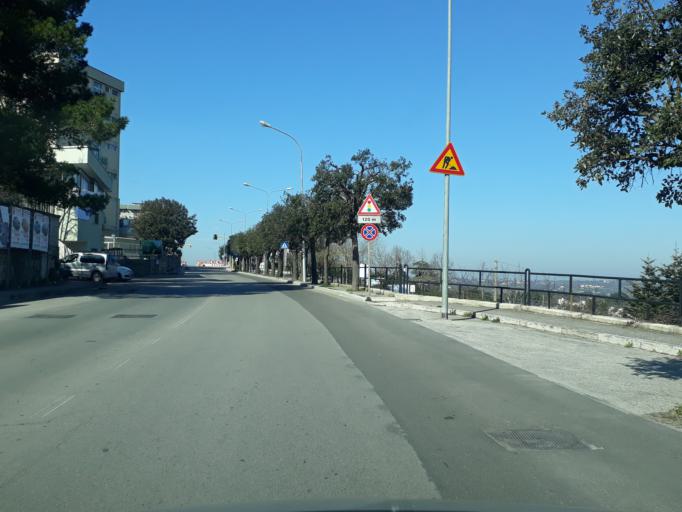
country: IT
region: Apulia
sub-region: Provincia di Taranto
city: Martina Franca
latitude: 40.7054
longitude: 17.3455
